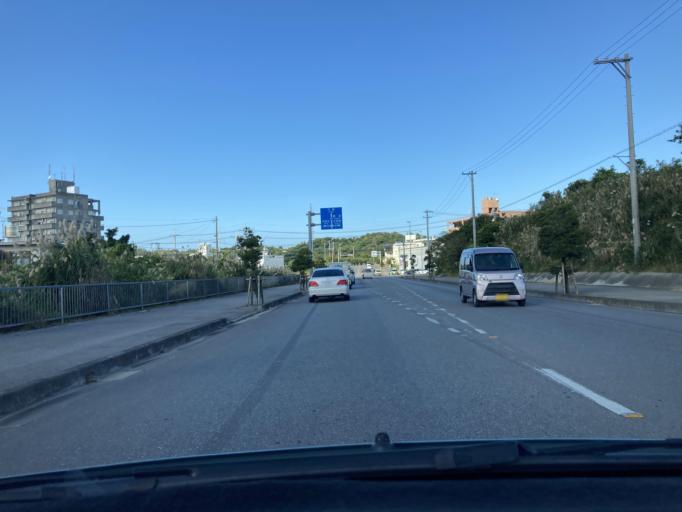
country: JP
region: Okinawa
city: Gushikawa
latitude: 26.3834
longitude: 127.8392
